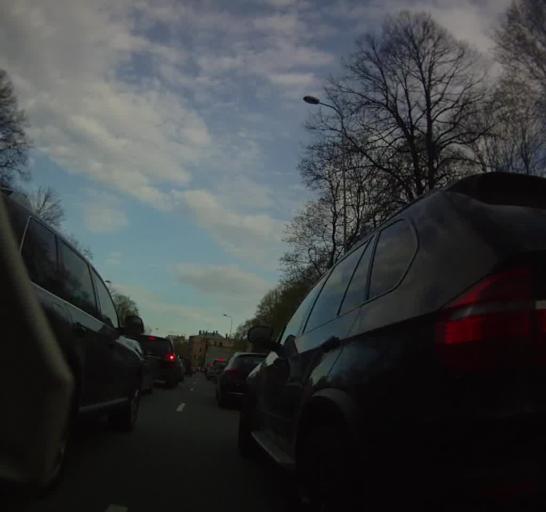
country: LV
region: Riga
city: Riga
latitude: 56.9692
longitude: 24.1414
